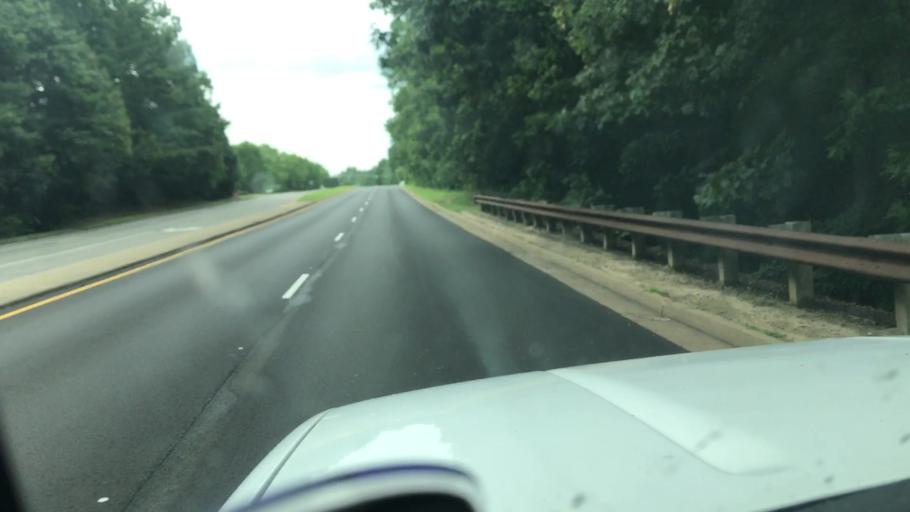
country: US
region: Virginia
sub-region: Henrico County
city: Short Pump
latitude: 37.6235
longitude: -77.5912
